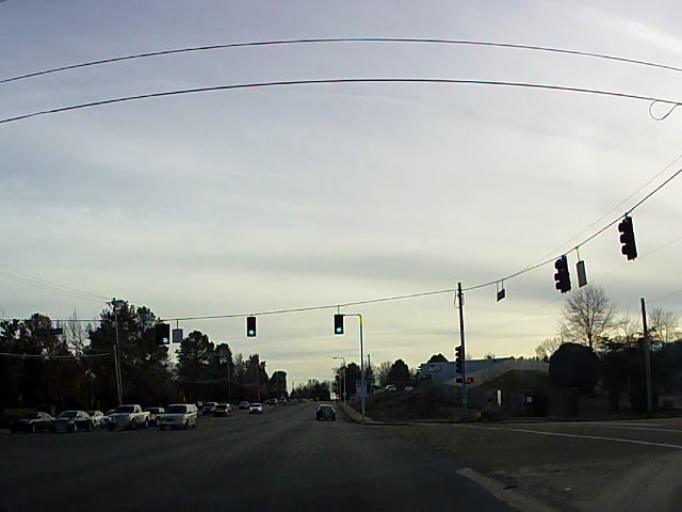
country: US
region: Tennessee
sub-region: Shelby County
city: Germantown
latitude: 35.0600
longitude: -89.8439
